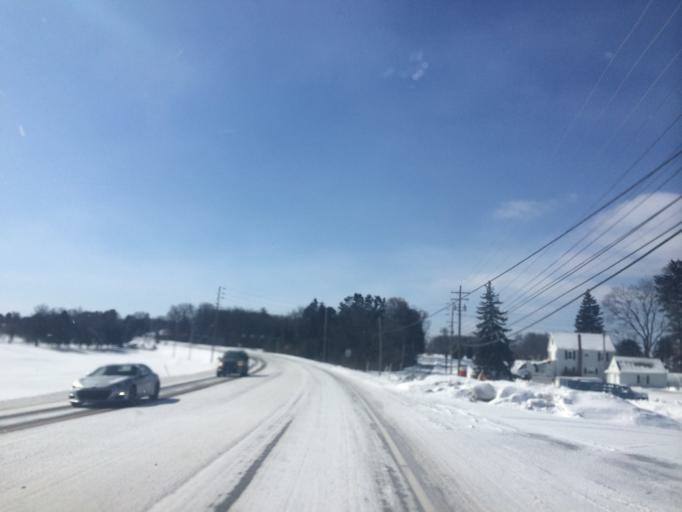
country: US
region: Pennsylvania
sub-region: Centre County
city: State College
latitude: 40.7764
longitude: -77.8852
